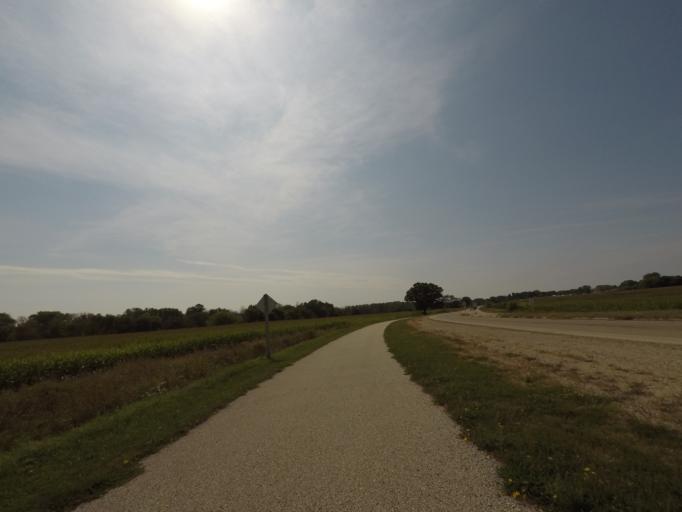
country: US
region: Wisconsin
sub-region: Jefferson County
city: Fort Atkinson
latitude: 42.9498
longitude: -88.8275
